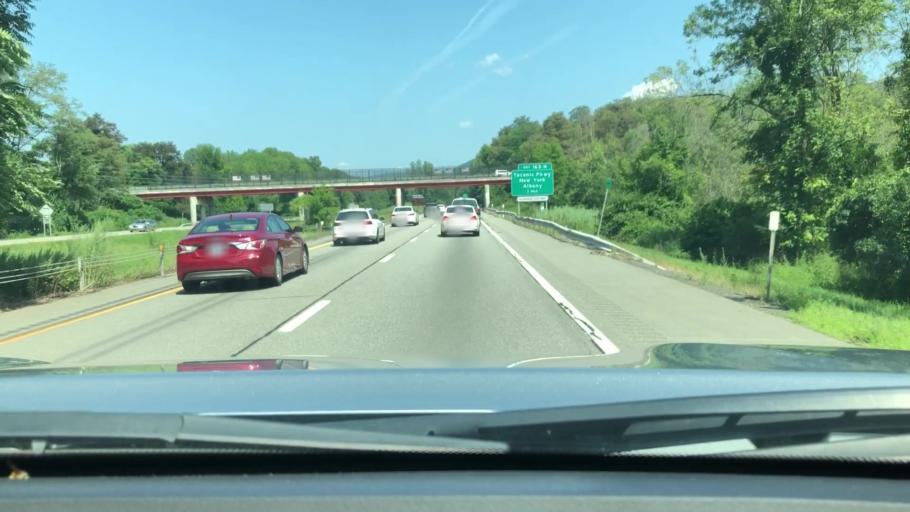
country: US
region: New York
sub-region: Dutchess County
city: Brinckerhoff
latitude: 41.5322
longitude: -73.7970
